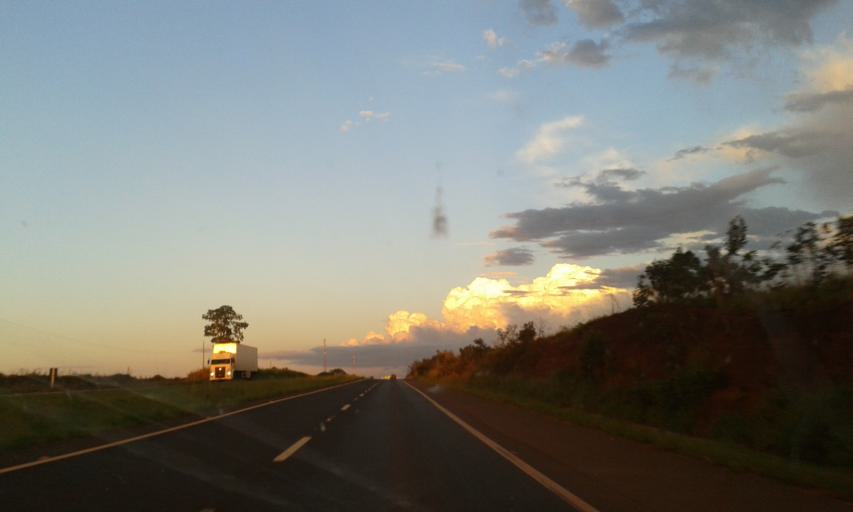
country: BR
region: Minas Gerais
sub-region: Monte Alegre De Minas
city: Monte Alegre de Minas
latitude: -18.8875
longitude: -48.7167
